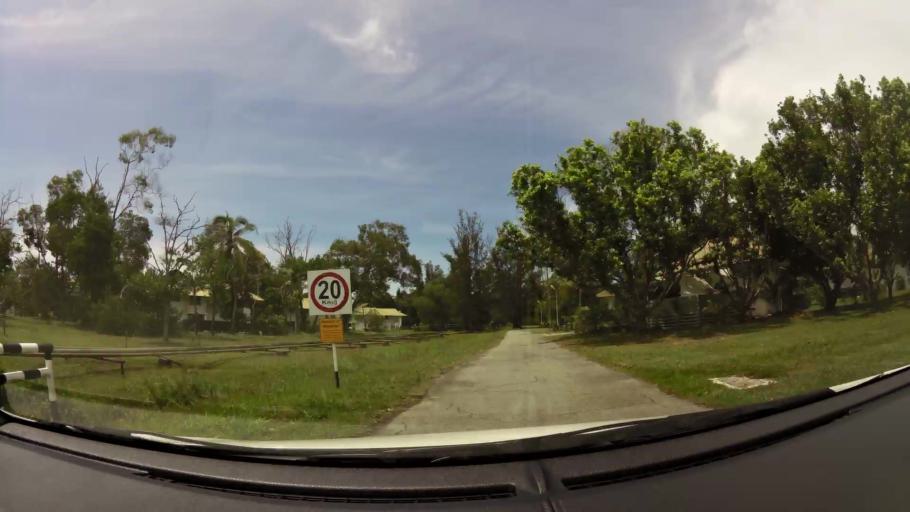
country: BN
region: Belait
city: Seria
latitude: 4.6056
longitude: 114.2885
